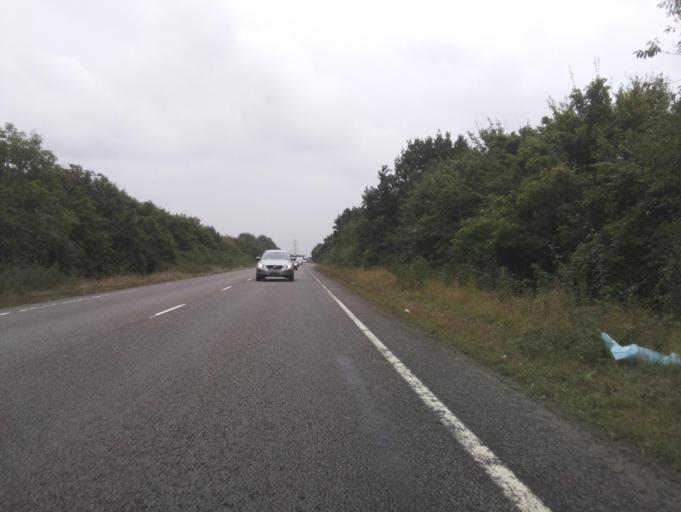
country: GB
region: England
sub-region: Nottinghamshire
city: South Collingham
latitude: 53.0903
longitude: -0.7626
